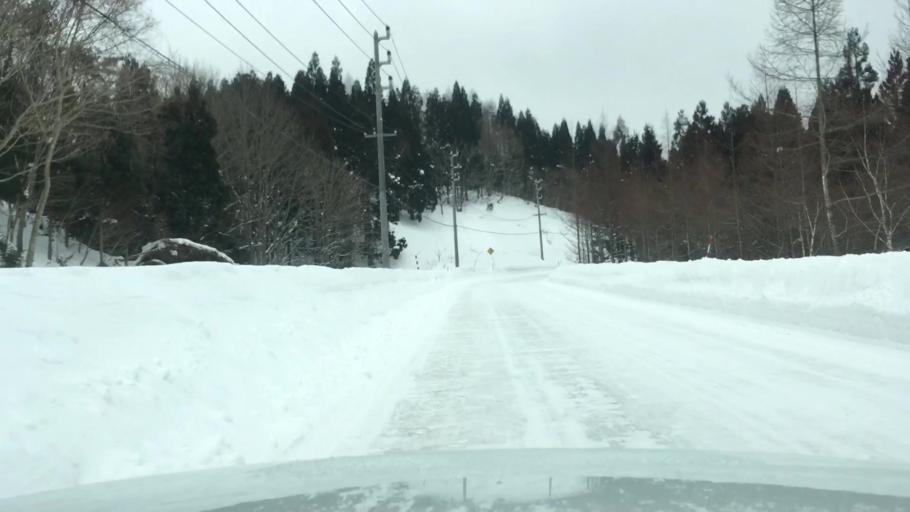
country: JP
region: Akita
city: Hanawa
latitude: 39.9999
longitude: 140.9875
